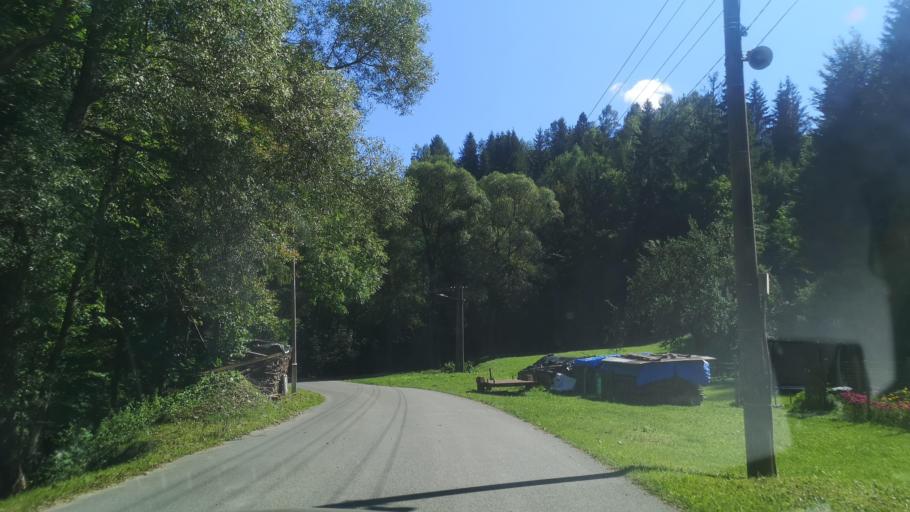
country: SK
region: Zilinsky
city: Oravska Lesna
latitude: 49.2892
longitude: 19.1305
